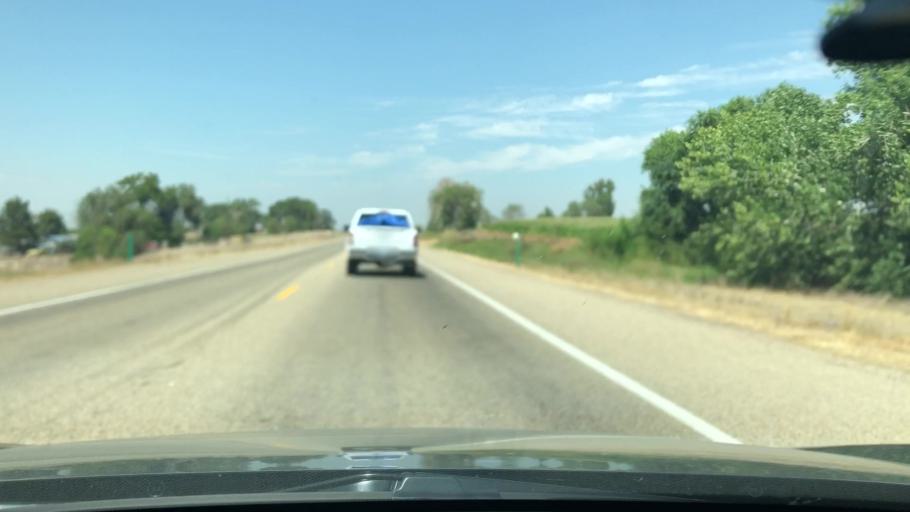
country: US
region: Idaho
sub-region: Canyon County
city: Parma
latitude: 43.8326
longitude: -116.9545
